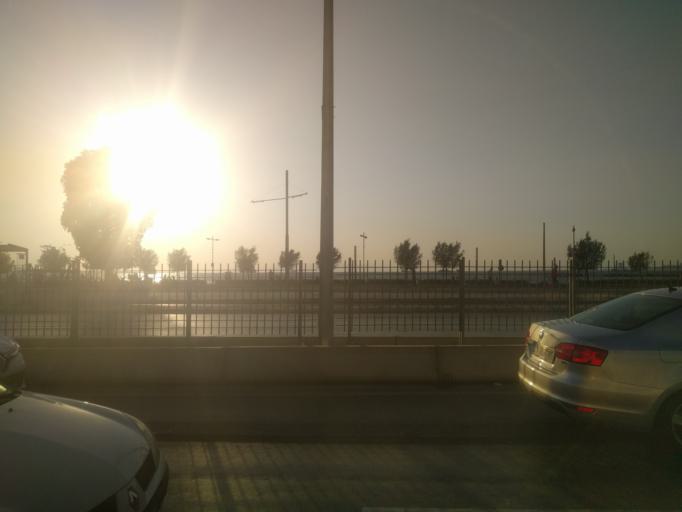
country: TR
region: Izmir
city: Izmir
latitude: 38.4201
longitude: 27.1282
